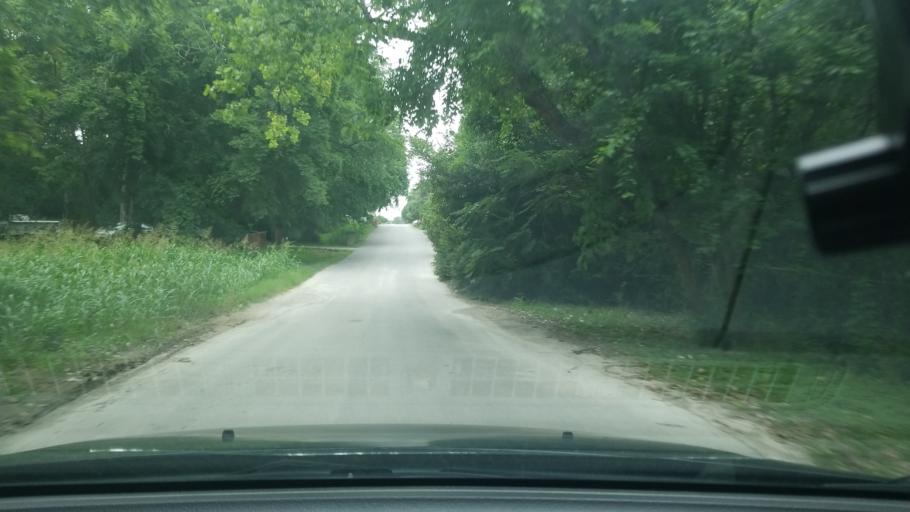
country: US
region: Texas
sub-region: Dallas County
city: Balch Springs
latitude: 32.7662
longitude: -96.6908
